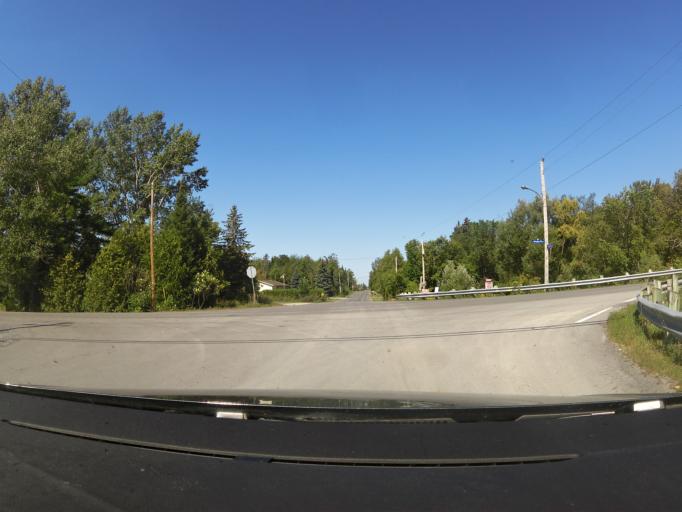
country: CA
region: Ontario
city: Bells Corners
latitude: 45.2765
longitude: -75.9977
